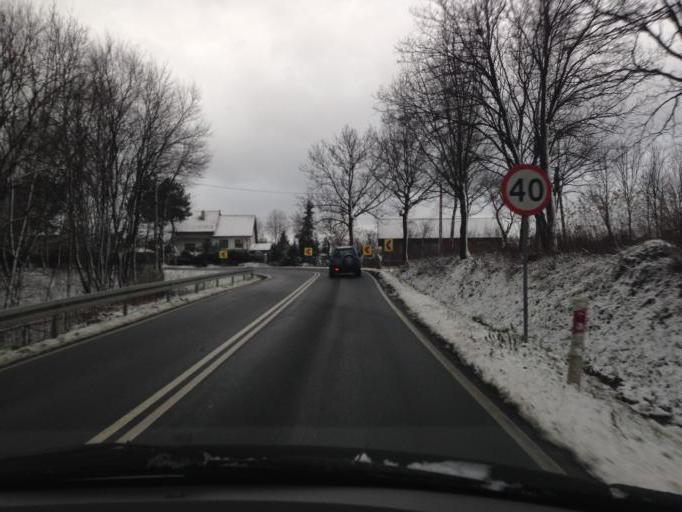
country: PL
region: Lesser Poland Voivodeship
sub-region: Powiat tarnowski
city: Siemiechow
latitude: 49.8462
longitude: 20.9321
